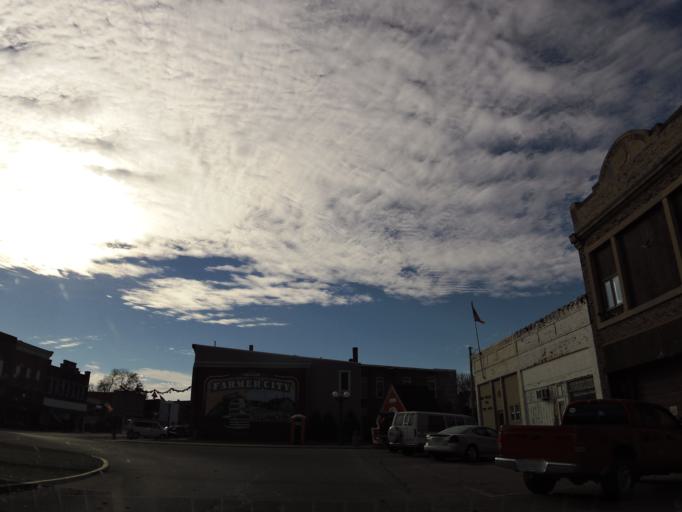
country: US
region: Illinois
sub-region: De Witt County
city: Farmer City
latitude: 40.2441
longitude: -88.6429
